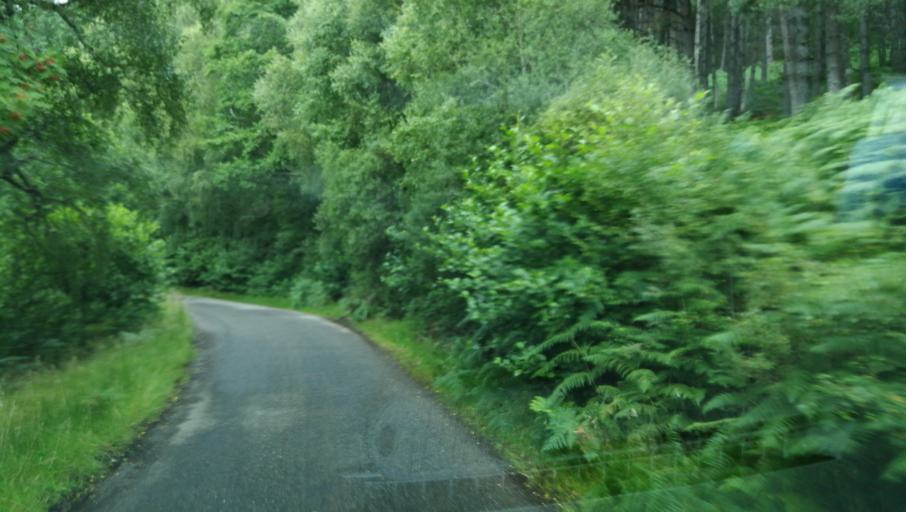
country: GB
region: Scotland
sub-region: Highland
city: Beauly
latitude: 57.3175
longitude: -4.8250
